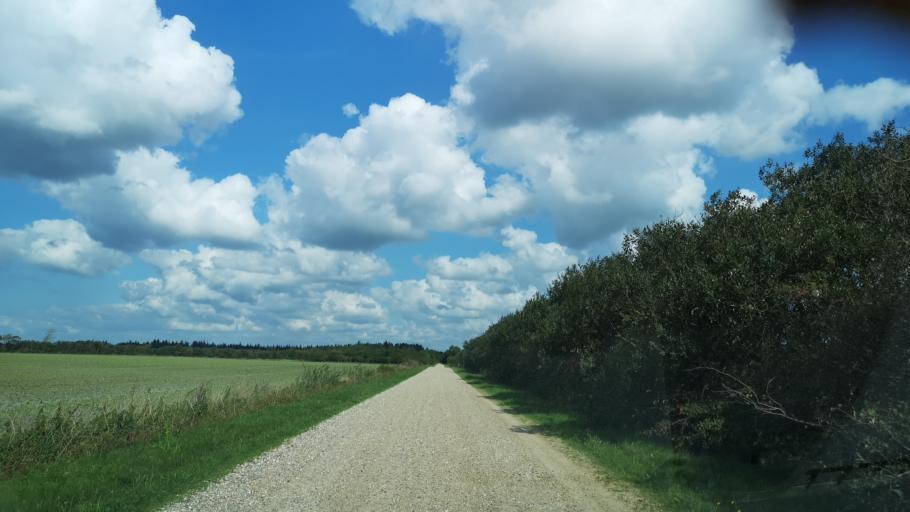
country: DK
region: Central Jutland
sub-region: Ringkobing-Skjern Kommune
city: Skjern
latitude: 55.8600
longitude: 8.3871
